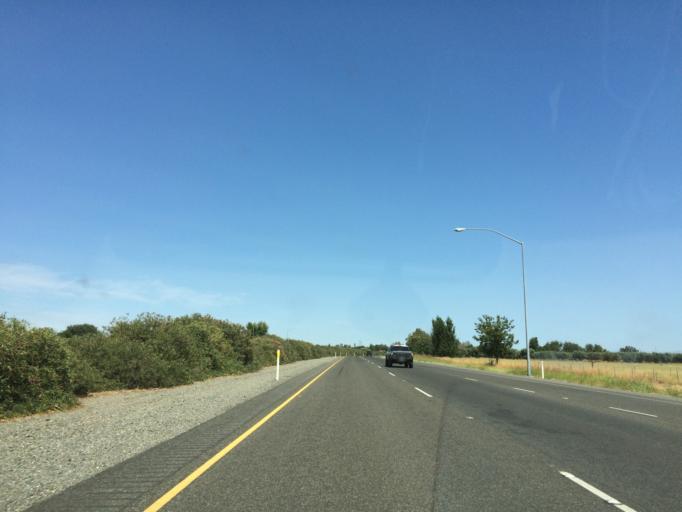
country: US
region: California
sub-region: Glenn County
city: Orland
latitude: 39.7836
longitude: -122.2042
